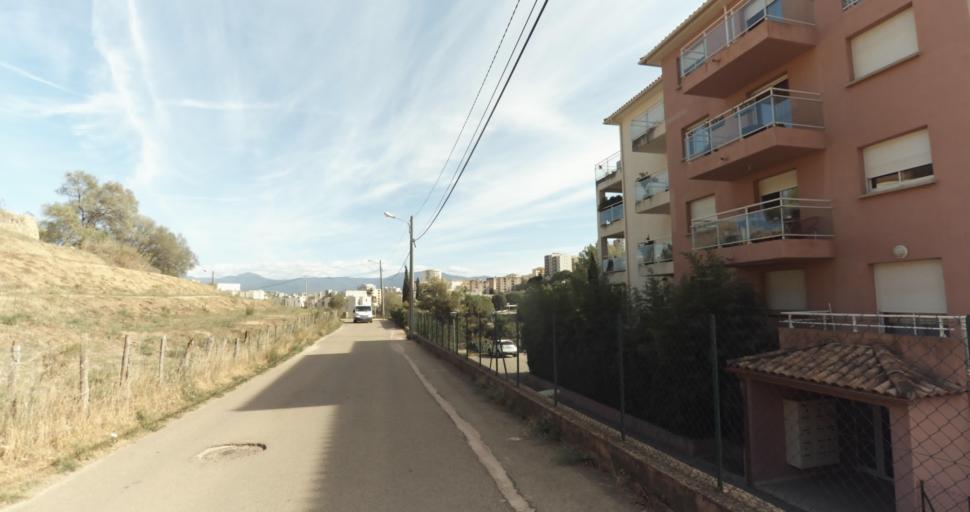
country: FR
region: Corsica
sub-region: Departement de la Corse-du-Sud
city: Ajaccio
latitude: 41.9376
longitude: 8.7313
